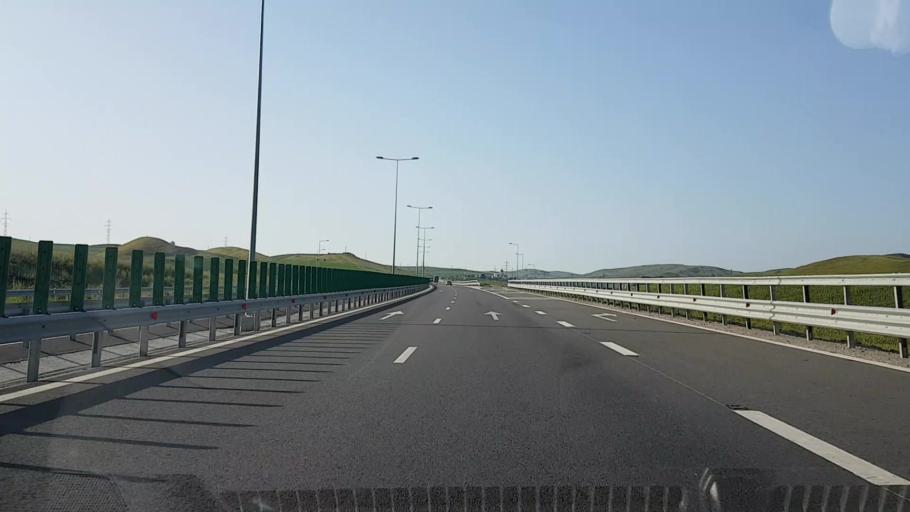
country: RO
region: Alba
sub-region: Comuna Unirea
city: Unirea
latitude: 46.4179
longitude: 23.7988
